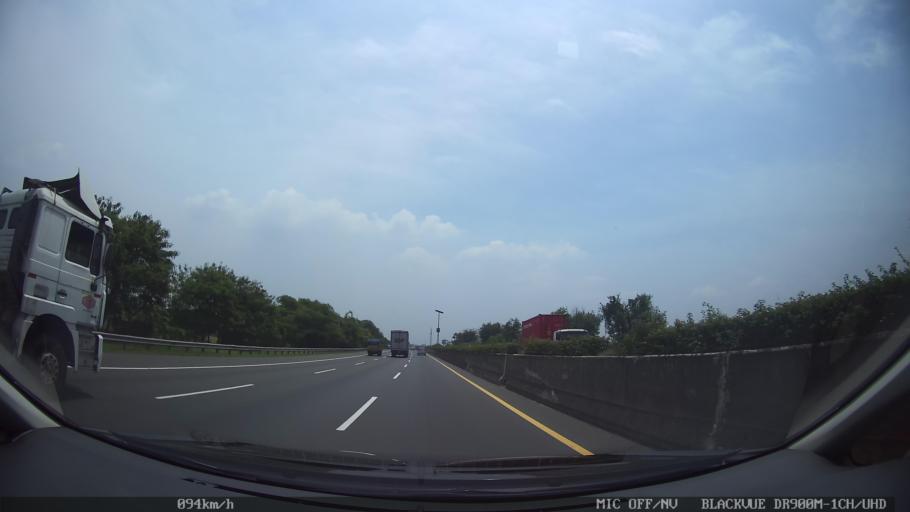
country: ID
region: West Java
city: Kresek
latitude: -6.1772
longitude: 106.3834
